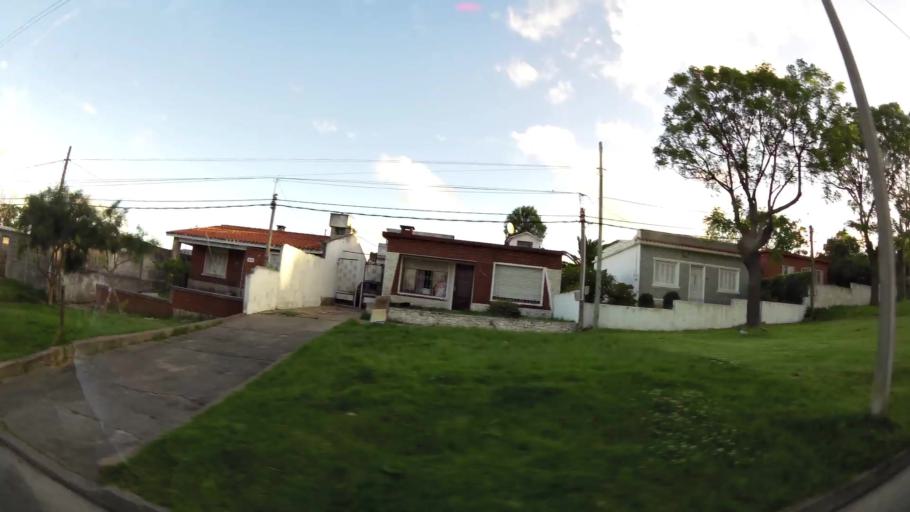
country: UY
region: Montevideo
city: Montevideo
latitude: -34.8839
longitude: -56.2556
